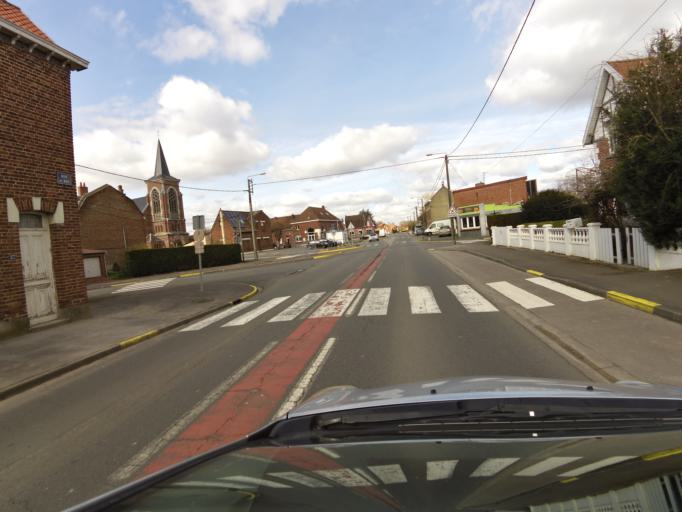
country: FR
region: Nord-Pas-de-Calais
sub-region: Departement du Pas-de-Calais
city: Lorgies
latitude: 50.5833
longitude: 2.7807
